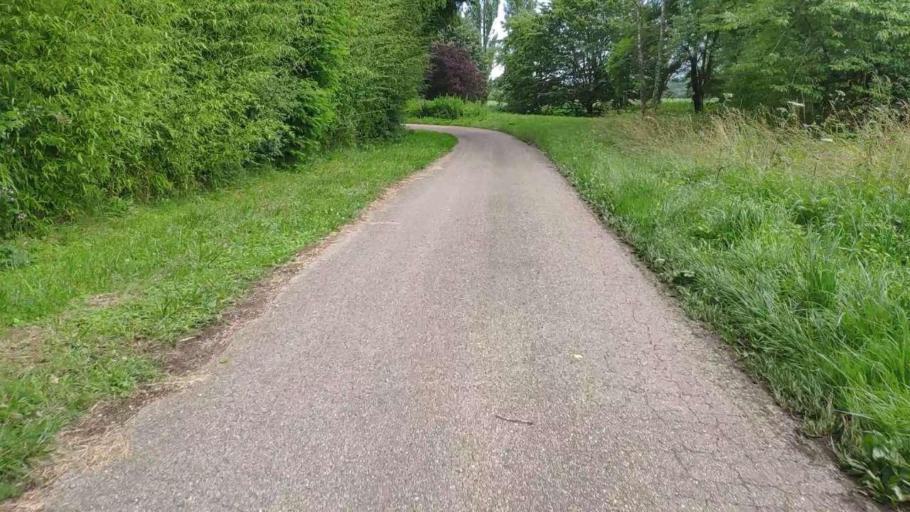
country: FR
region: Franche-Comte
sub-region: Departement du Jura
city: Chaussin
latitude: 46.8676
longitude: 5.4314
